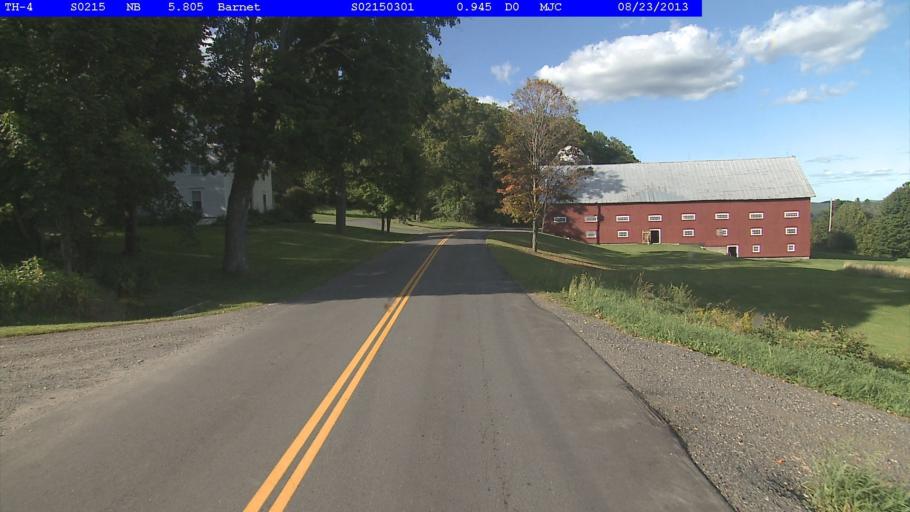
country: US
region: New Hampshire
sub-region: Grafton County
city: Woodsville
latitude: 44.2876
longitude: -72.1696
